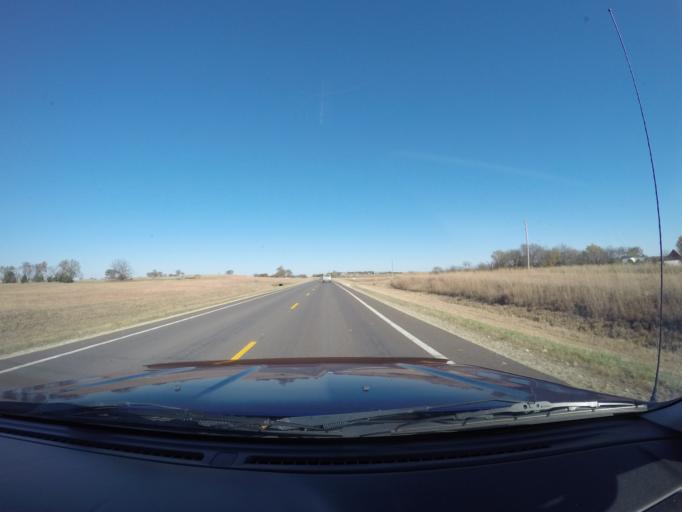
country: US
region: Kansas
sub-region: Marshall County
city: Blue Rapids
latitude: 39.5111
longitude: -96.7553
